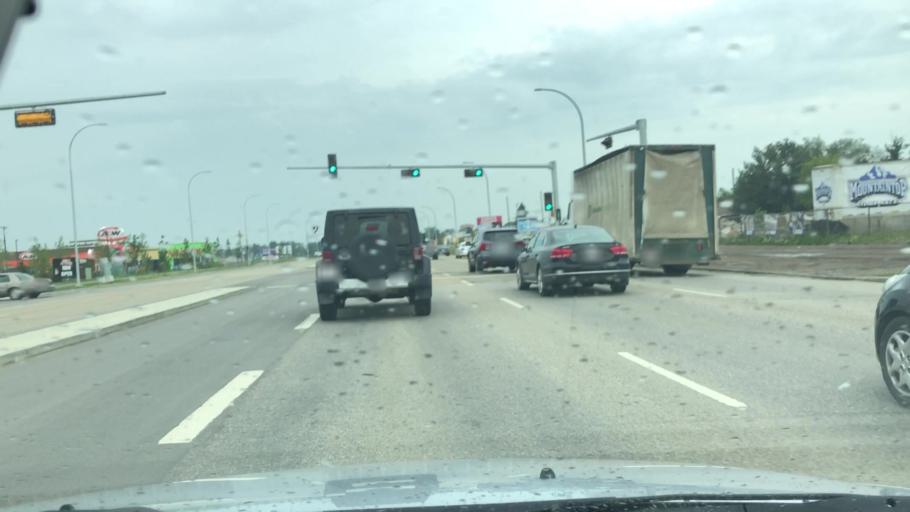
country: CA
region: Alberta
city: St. Albert
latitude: 53.6019
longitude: -113.5771
